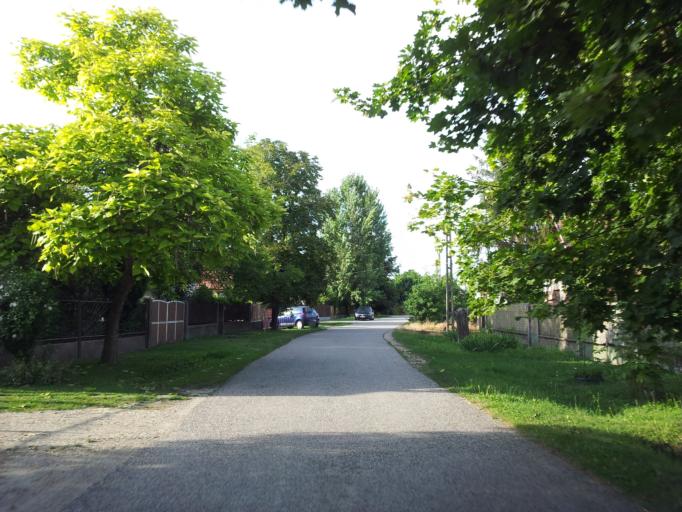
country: HU
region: Pest
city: Kiskunlachaza
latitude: 47.1820
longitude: 19.0087
